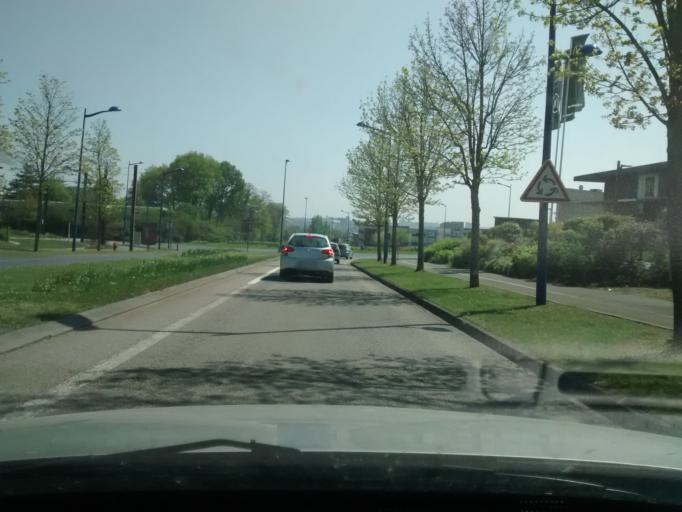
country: FR
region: Pays de la Loire
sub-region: Departement de la Sarthe
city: La Chapelle-Saint-Aubin
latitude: 48.0148
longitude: 0.1598
